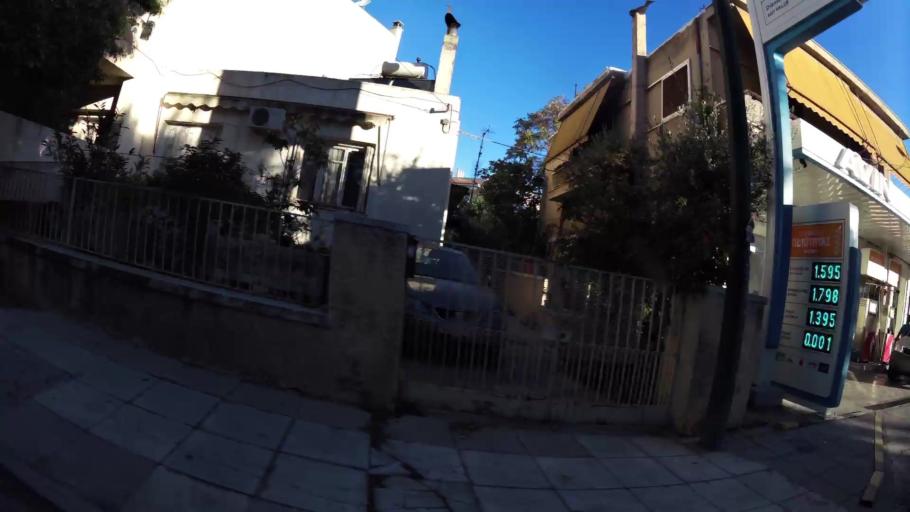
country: GR
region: Attica
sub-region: Nomarchia Athinas
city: Khalandrion
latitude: 38.0197
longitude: 23.8103
